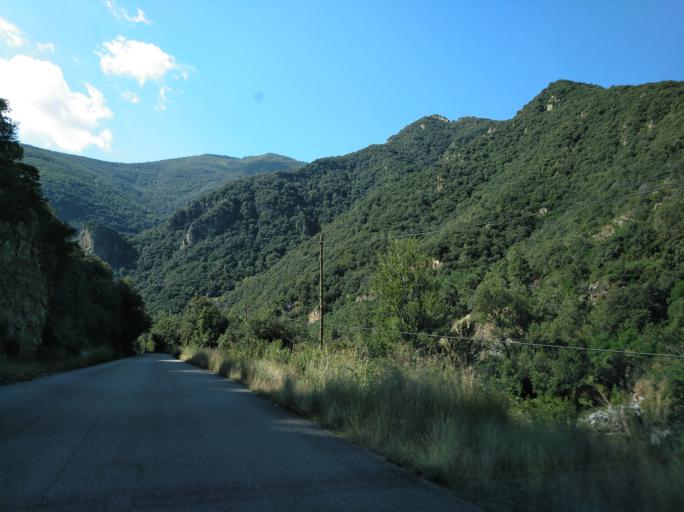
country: ES
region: Catalonia
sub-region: Provincia de Girona
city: Susqueda
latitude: 41.9909
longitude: 2.5702
